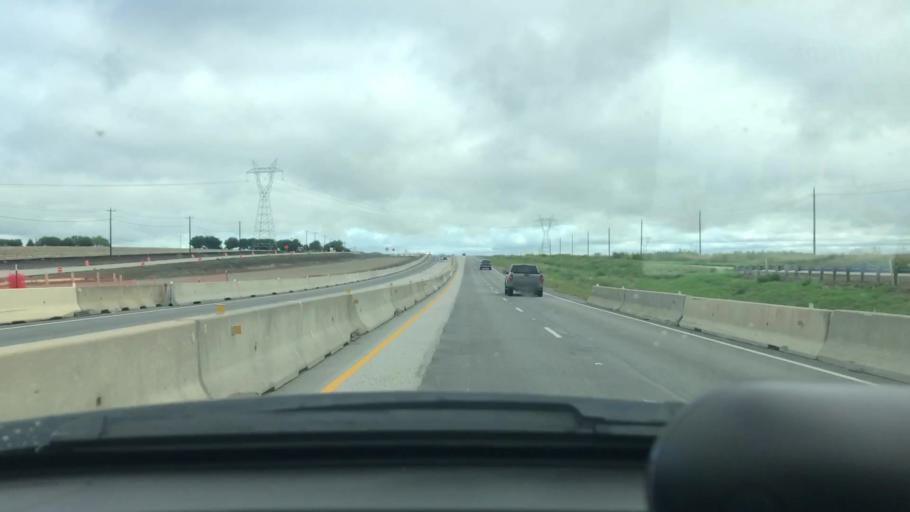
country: US
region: Texas
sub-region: Collin County
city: Anna
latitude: 33.3658
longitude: -96.5828
